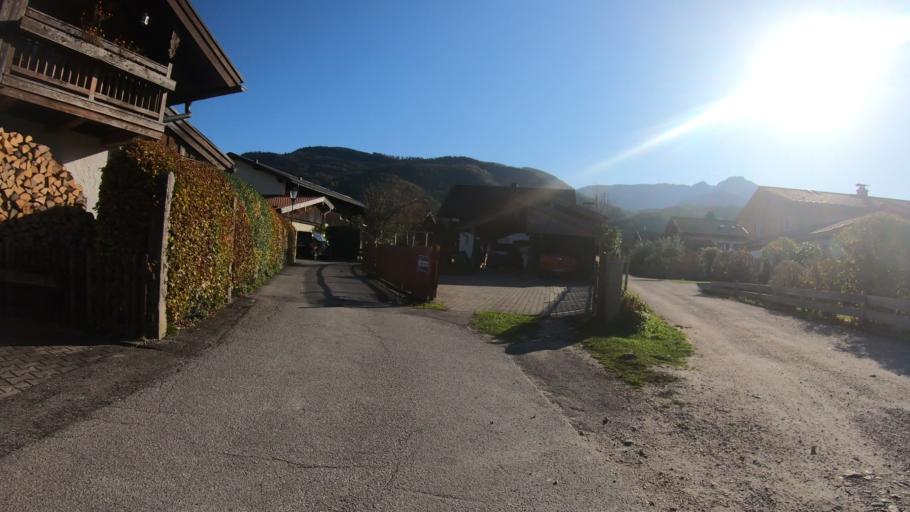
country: DE
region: Bavaria
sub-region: Upper Bavaria
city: Bergen
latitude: 47.8044
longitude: 12.5890
